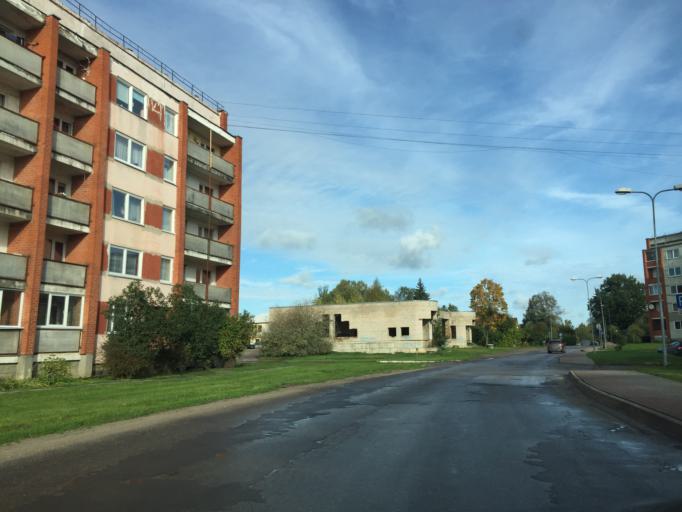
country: LV
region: Dobeles Rajons
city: Dobele
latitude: 56.6200
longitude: 23.2873
